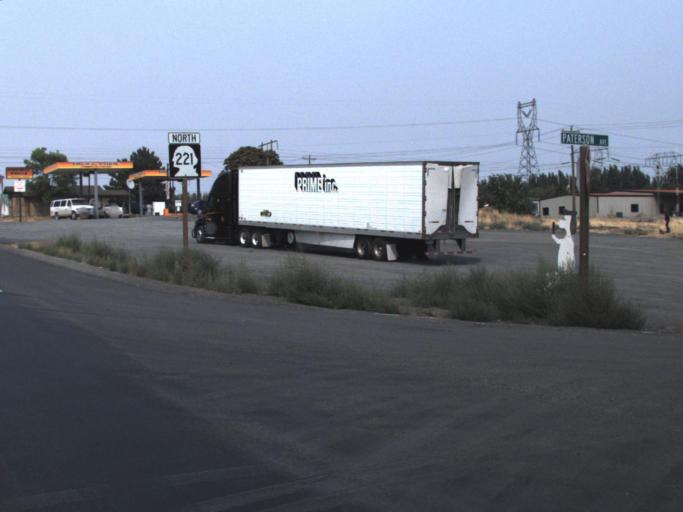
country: US
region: Oregon
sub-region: Morrow County
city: Irrigon
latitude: 45.9391
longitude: -119.6031
